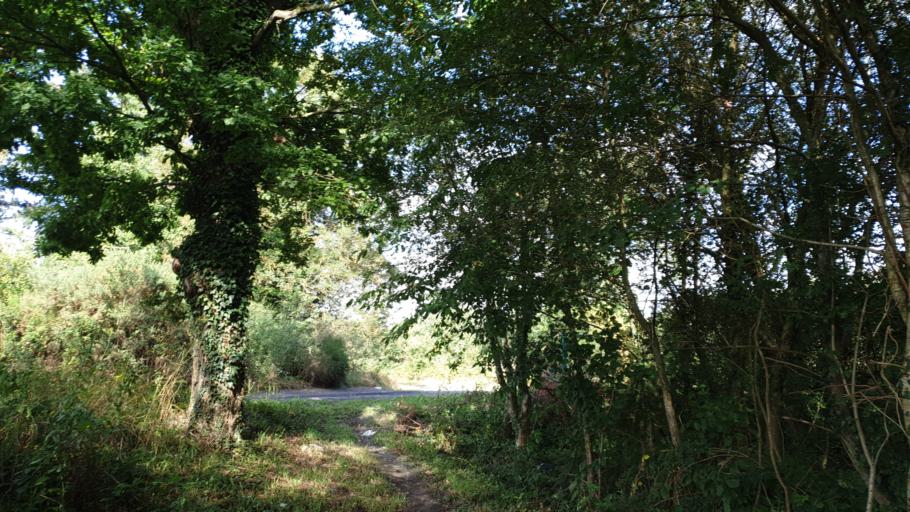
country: FR
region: Brittany
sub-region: Departement d'Ille-et-Vilaine
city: Bain-de-Bretagne
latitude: 47.8615
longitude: -1.6875
